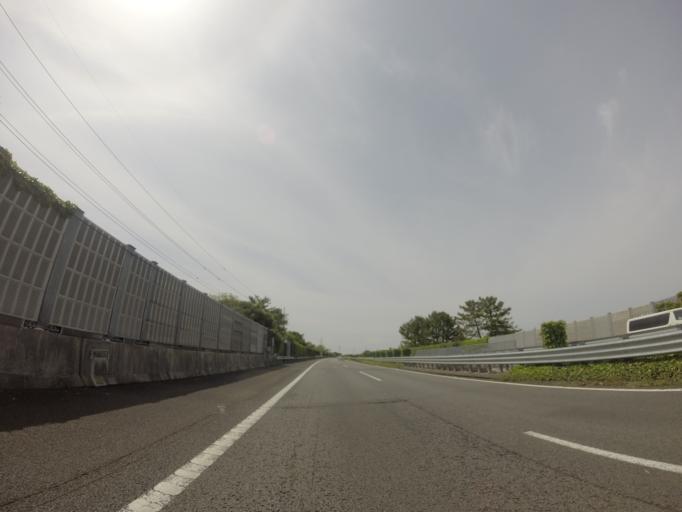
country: JP
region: Shizuoka
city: Fujieda
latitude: 34.8418
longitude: 138.2818
